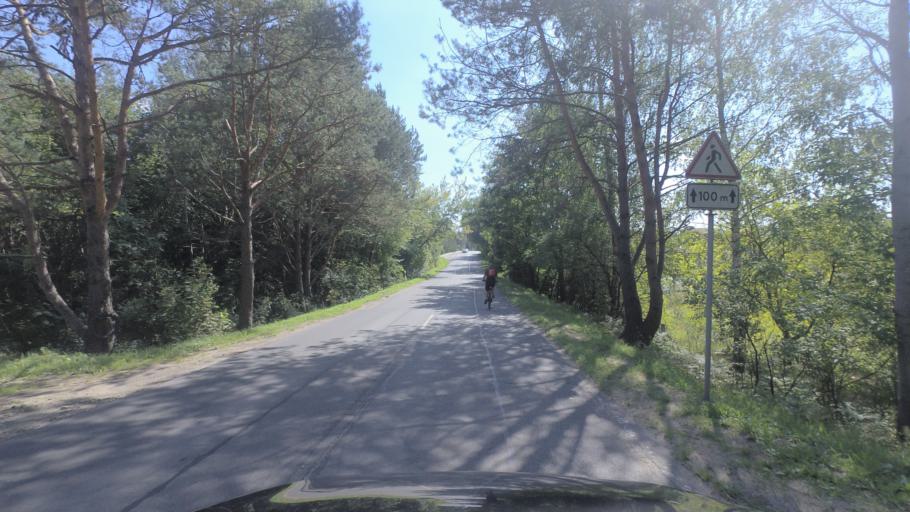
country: LT
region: Vilnius County
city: Rasos
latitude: 54.7933
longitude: 25.3507
